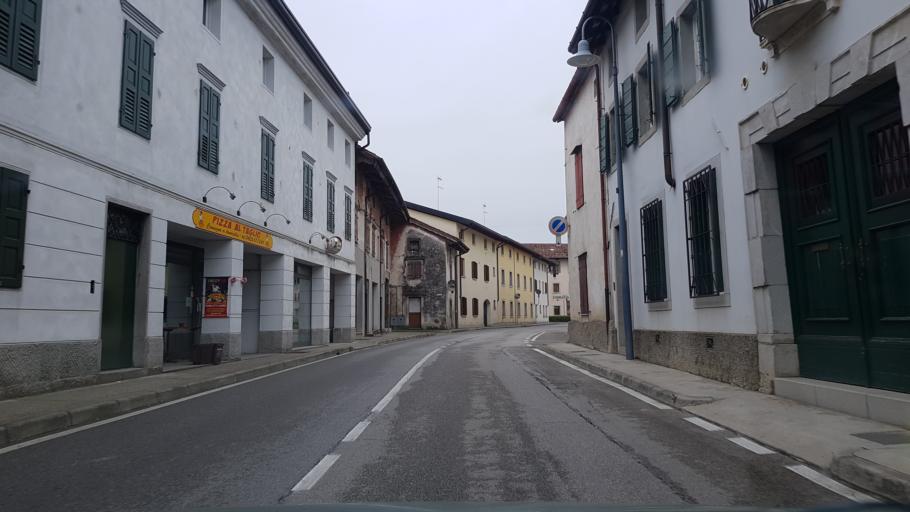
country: IT
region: Friuli Venezia Giulia
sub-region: Provincia di Udine
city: Pradamano
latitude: 46.0322
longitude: 13.3050
